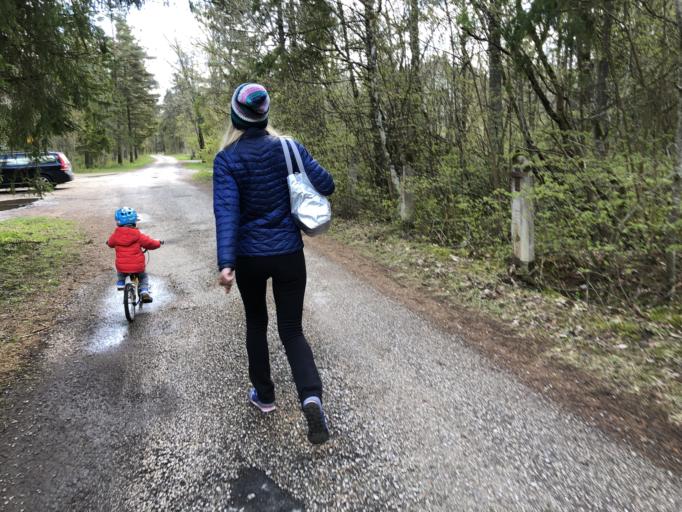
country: EE
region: Harju
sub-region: Harku vald
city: Tabasalu
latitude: 59.4369
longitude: 24.5366
